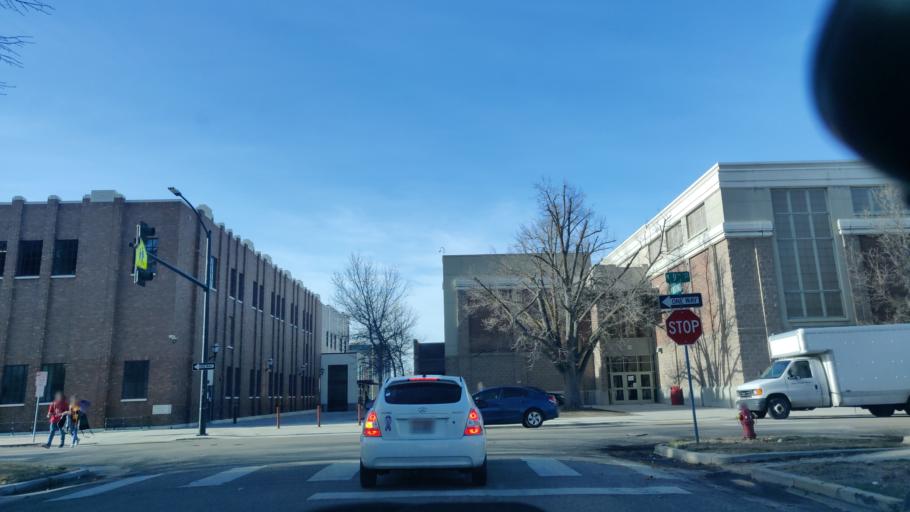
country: US
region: Idaho
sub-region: Ada County
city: Boise
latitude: 43.6200
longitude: -116.2007
